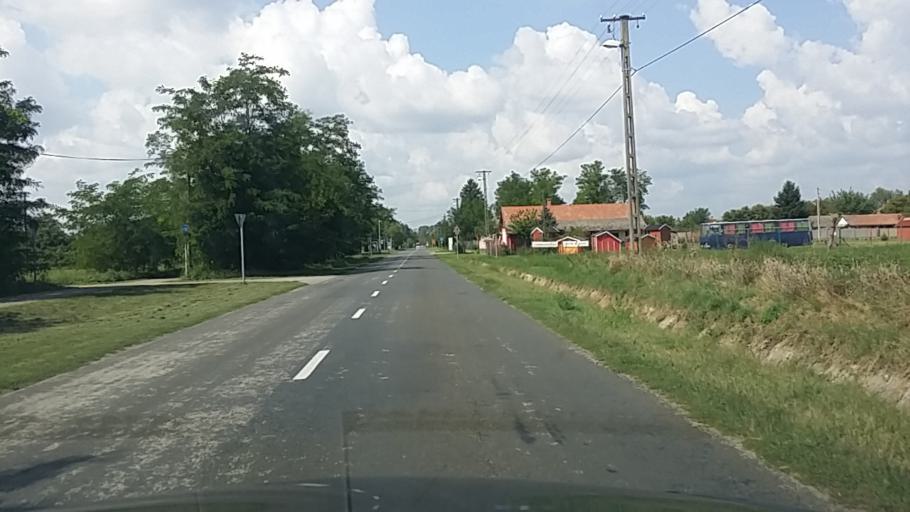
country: HU
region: Bacs-Kiskun
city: Tiszaalpar
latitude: 46.7496
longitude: 20.0399
